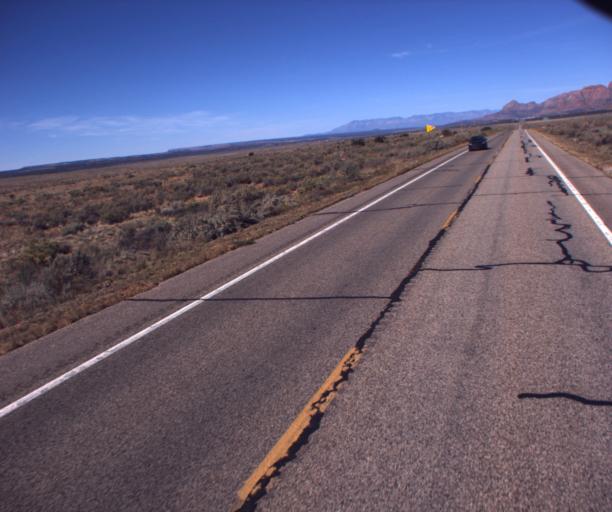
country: US
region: Arizona
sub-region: Mohave County
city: Colorado City
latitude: 36.9010
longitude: -112.9197
